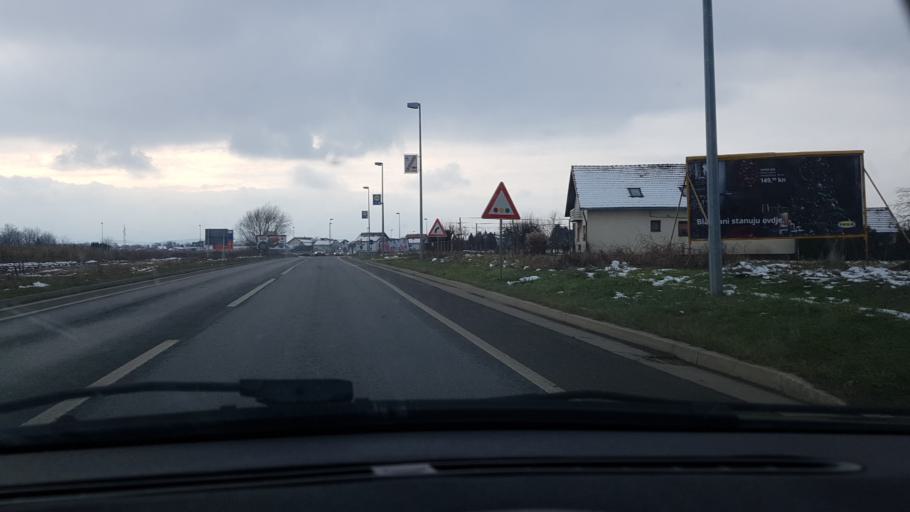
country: HR
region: Varazdinska
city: Jalkovec
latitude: 46.2941
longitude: 16.3088
